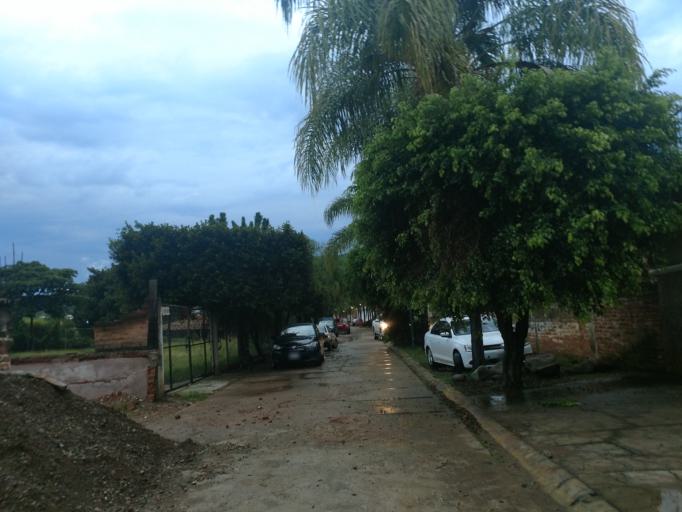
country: MX
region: Jalisco
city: Talpa de Allende
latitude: 20.3799
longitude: -104.8219
